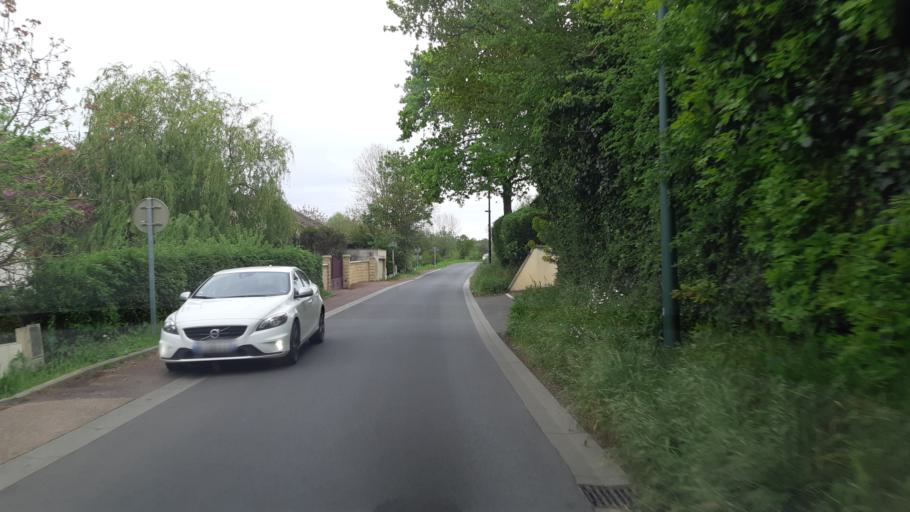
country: FR
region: Lower Normandy
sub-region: Departement de la Manche
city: Donville-les-Bains
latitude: 48.8520
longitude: -1.5537
